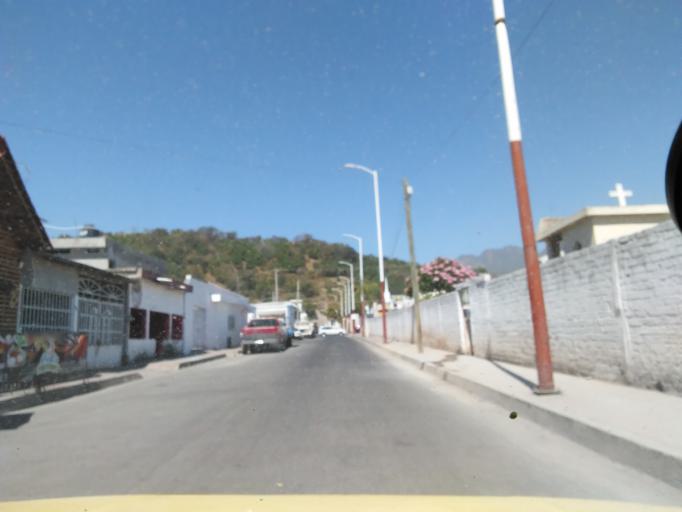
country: MX
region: Nayarit
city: Xalisco
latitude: 21.4384
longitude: -104.8985
